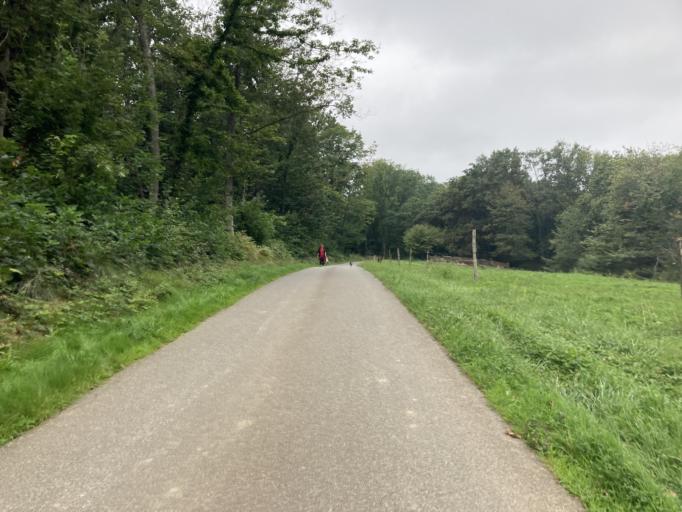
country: FR
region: Aquitaine
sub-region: Departement des Pyrenees-Atlantiques
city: Ledeuix
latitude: 43.2610
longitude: -0.6283
